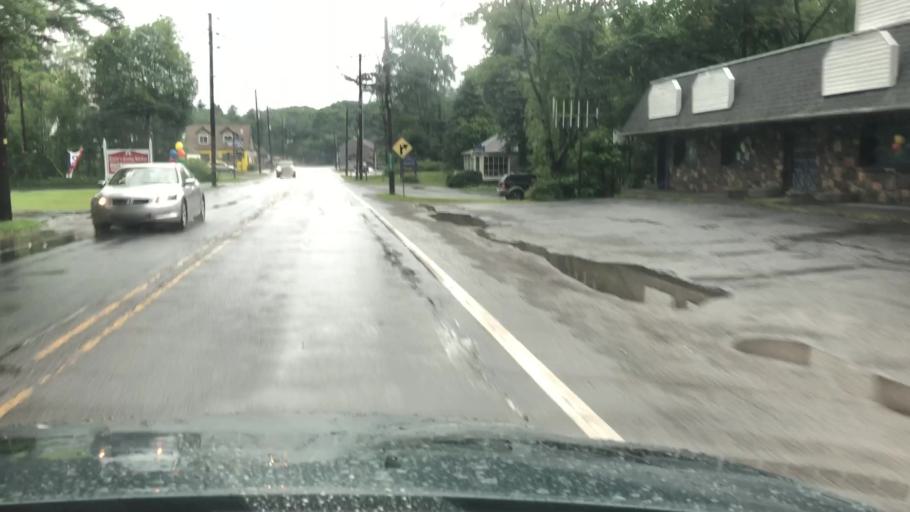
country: US
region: Pennsylvania
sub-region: Monroe County
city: Mountainhome
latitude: 41.1786
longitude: -75.2694
